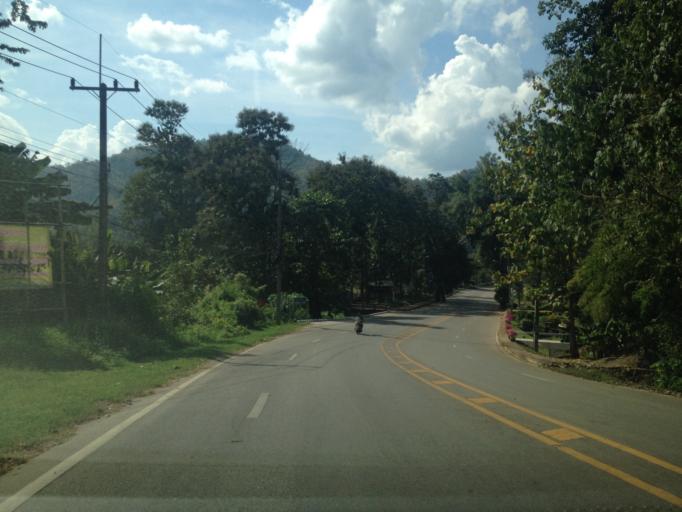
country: TH
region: Chiang Mai
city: Samoeng
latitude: 18.8477
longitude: 98.7352
